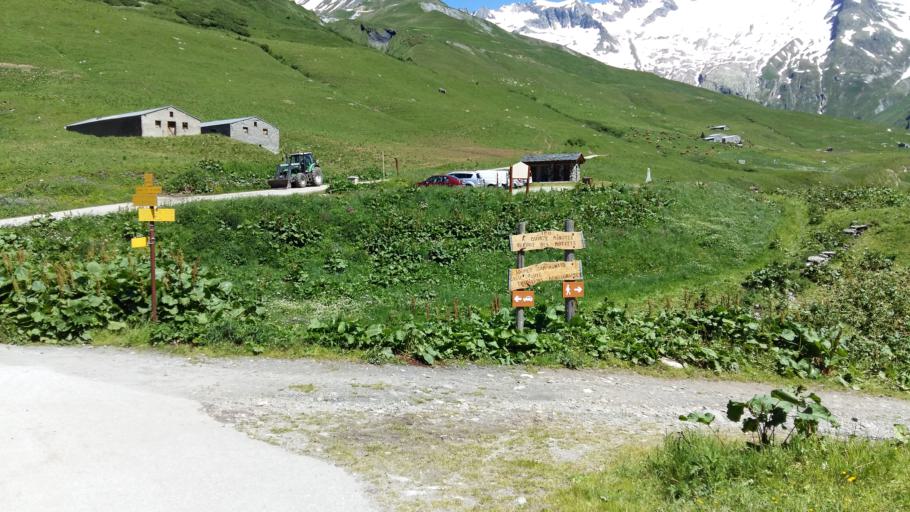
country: FR
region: Rhone-Alpes
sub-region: Departement de la Haute-Savoie
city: Les Contamines-Montjoie
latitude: 45.7274
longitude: 6.7676
